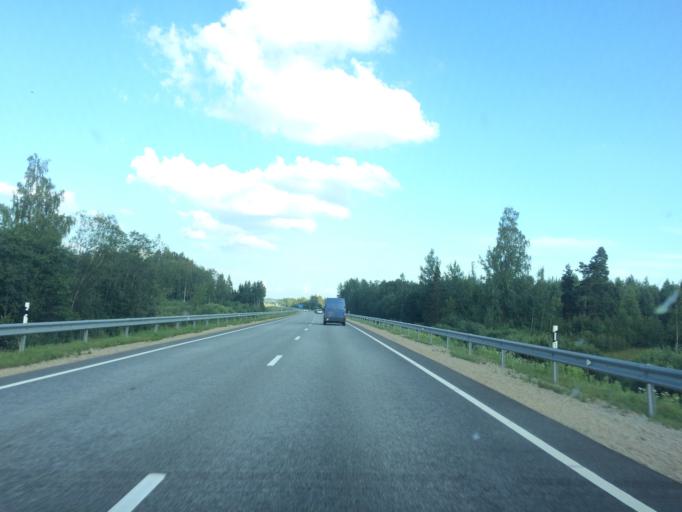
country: LV
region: Skriveri
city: Skriveri
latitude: 56.7378
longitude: 25.1400
